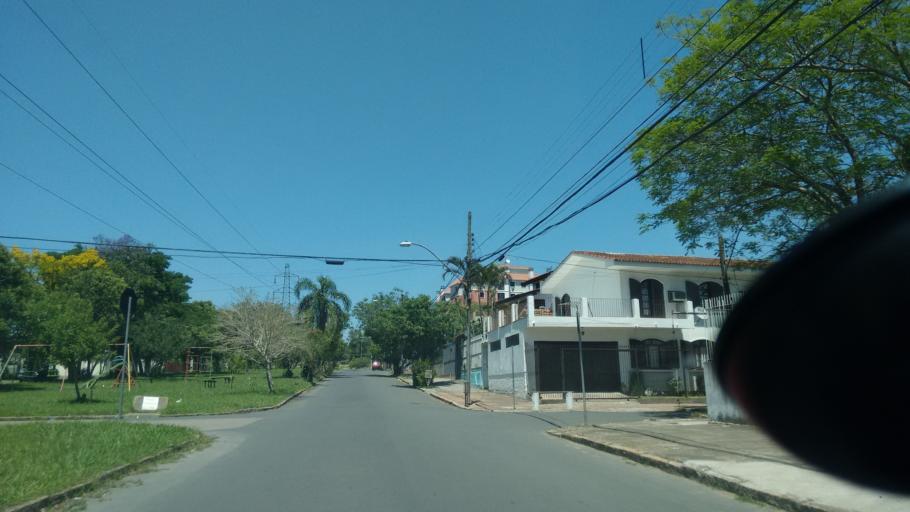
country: BR
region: Rio Grande do Sul
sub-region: Cachoeirinha
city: Cachoeirinha
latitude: -29.9999
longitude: -51.1269
